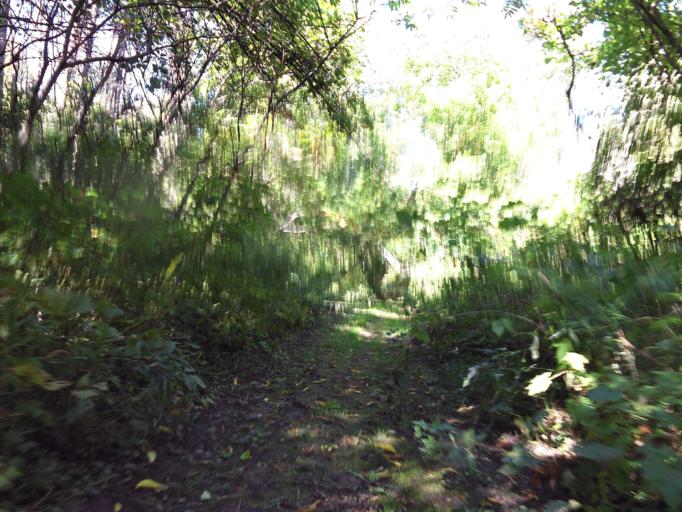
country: CA
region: Ontario
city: Casselman
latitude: 45.2692
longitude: -75.2824
